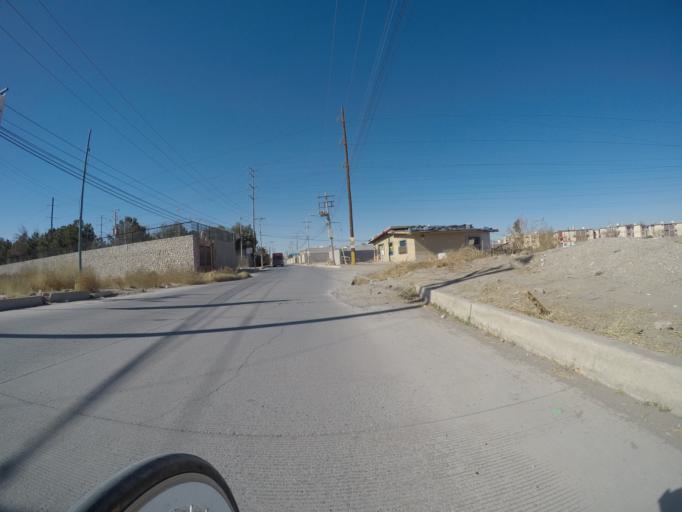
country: MX
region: Chihuahua
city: Ciudad Juarez
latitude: 31.6951
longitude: -106.4004
